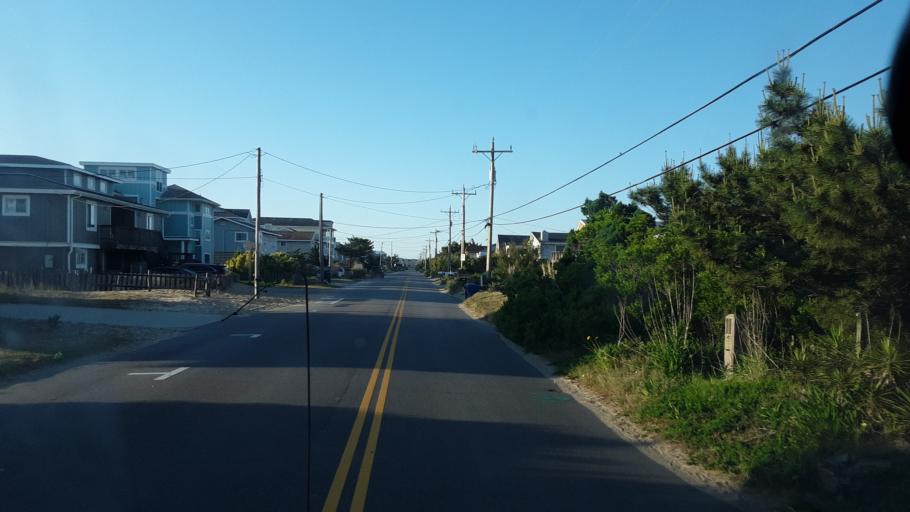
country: US
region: Virginia
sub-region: City of Virginia Beach
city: Virginia Beach
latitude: 36.7127
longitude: -75.9318
